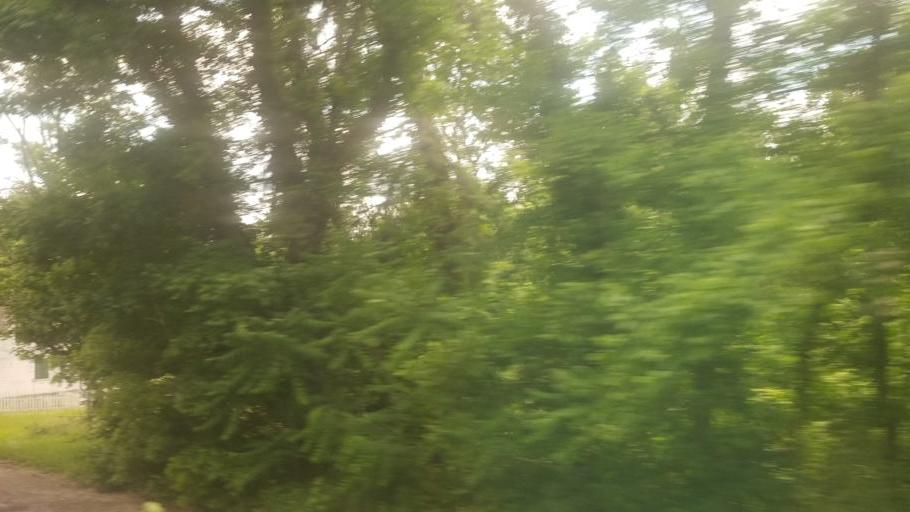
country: US
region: Maryland
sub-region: Frederick County
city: Point of Rocks
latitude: 39.3072
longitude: -77.5582
